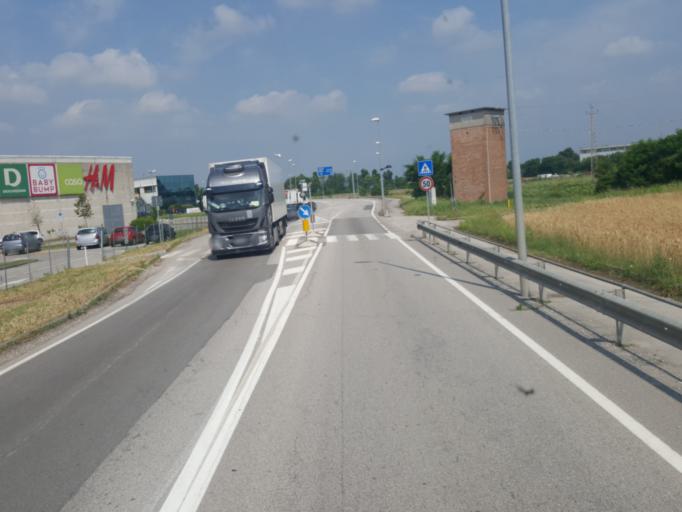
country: IT
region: Veneto
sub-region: Provincia di Treviso
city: Lancenigo-Villorba
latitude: 45.7431
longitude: 12.2540
